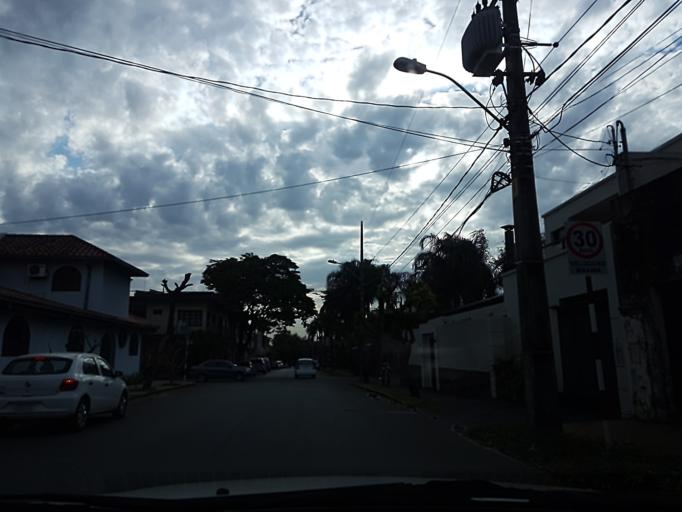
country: PY
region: Asuncion
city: Asuncion
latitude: -25.2995
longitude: -57.5862
